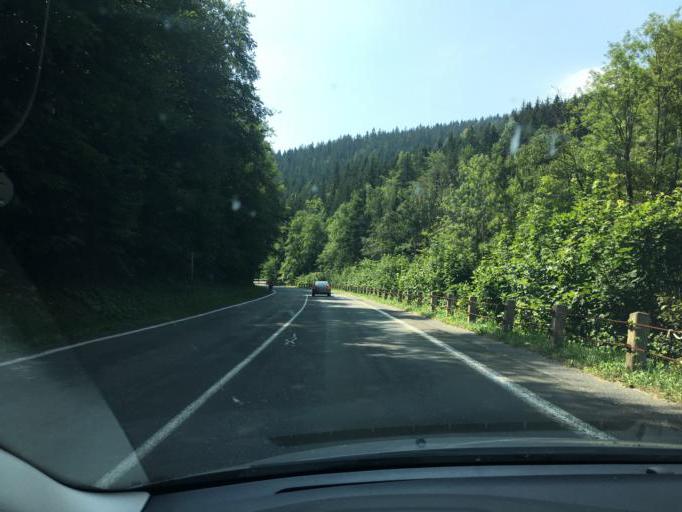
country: CZ
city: Benecko
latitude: 50.6872
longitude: 15.5782
